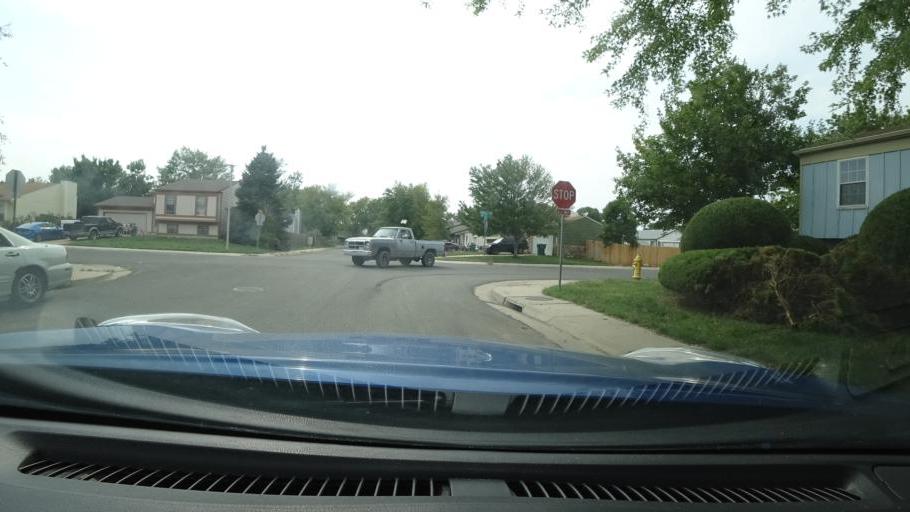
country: US
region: Colorado
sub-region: Adams County
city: Aurora
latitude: 39.7487
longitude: -104.7668
